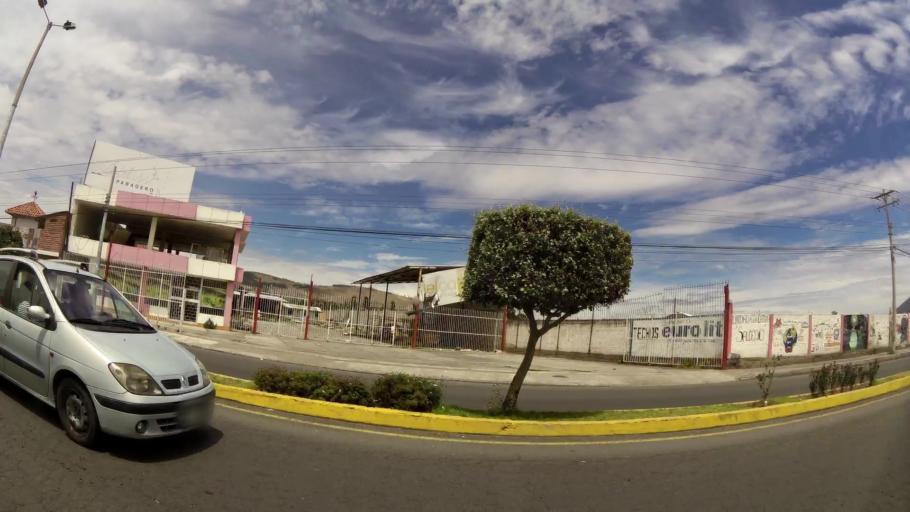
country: EC
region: Cotopaxi
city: San Miguel de Salcedo
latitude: -1.0478
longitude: -78.5938
